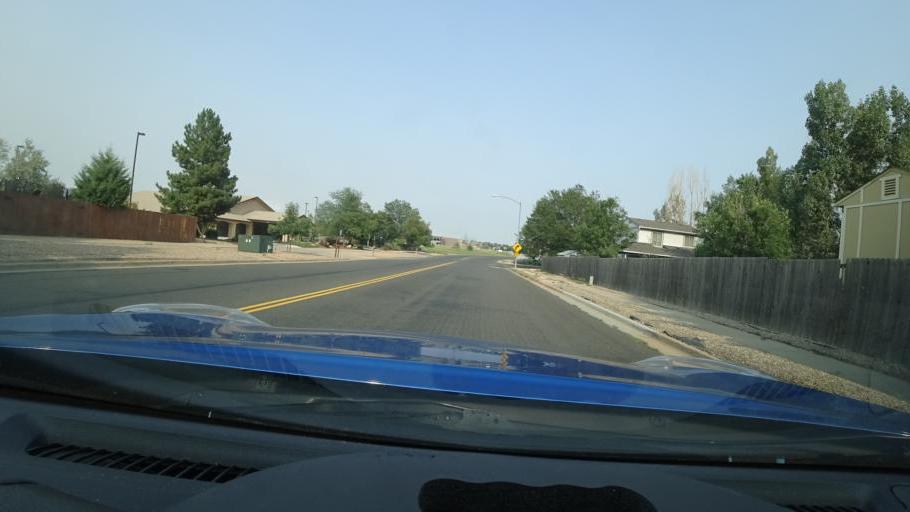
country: US
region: Colorado
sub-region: Adams County
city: Aurora
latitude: 39.6675
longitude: -104.7813
